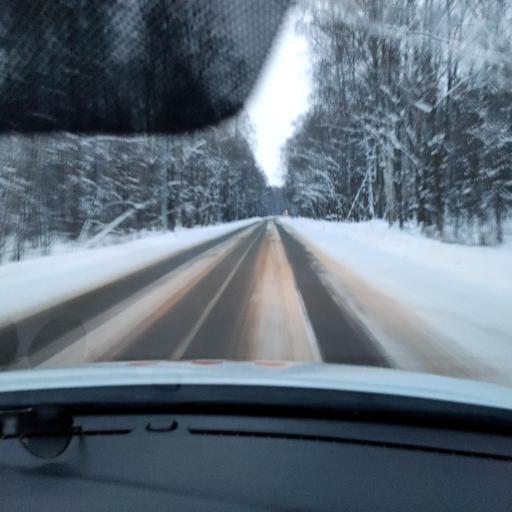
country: RU
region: Tatarstan
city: Vysokaya Gora
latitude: 55.9333
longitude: 49.1687
